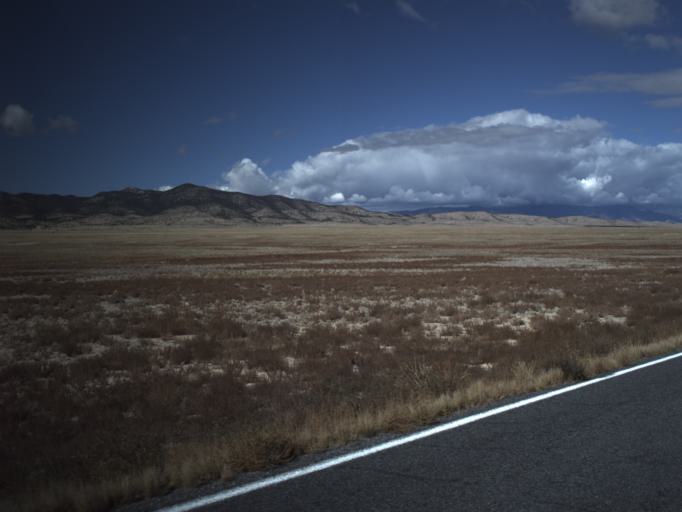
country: US
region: Utah
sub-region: Beaver County
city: Milford
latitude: 38.6342
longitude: -113.8565
